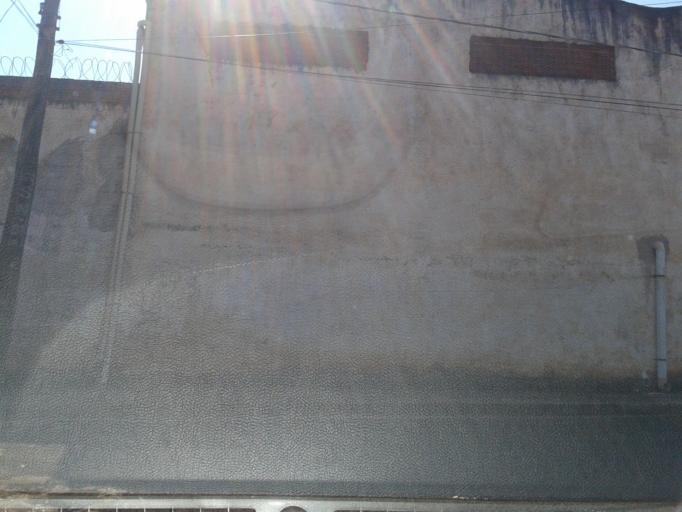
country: BR
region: Minas Gerais
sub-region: Ituiutaba
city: Ituiutaba
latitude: -18.9551
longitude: -49.4541
